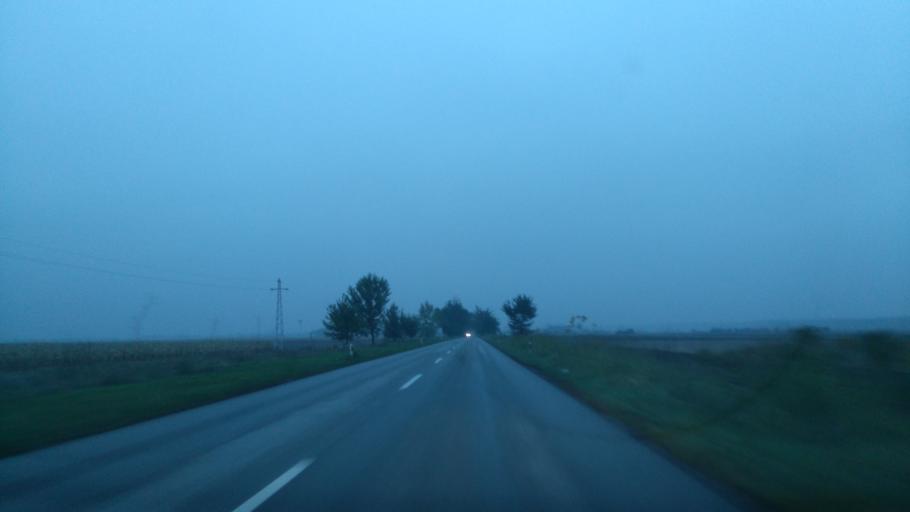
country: RS
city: Backo Petrovo Selo
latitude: 45.6804
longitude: 20.0676
